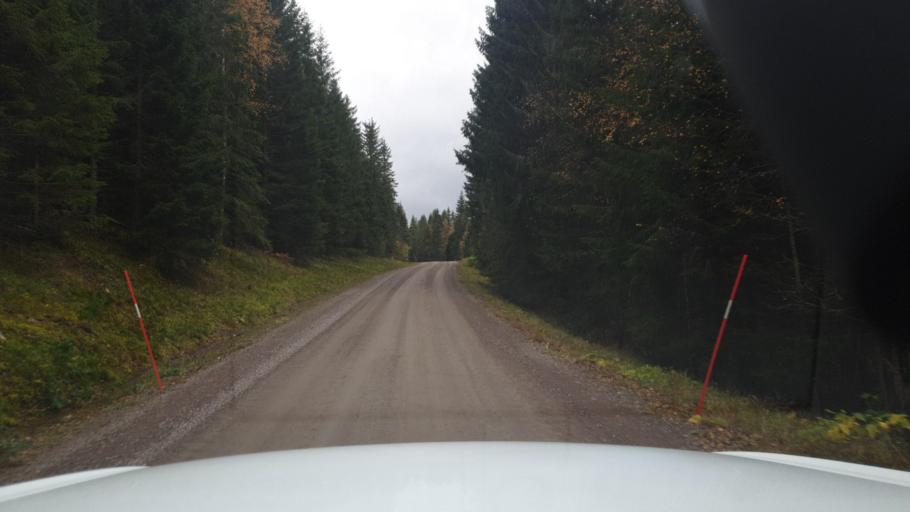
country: SE
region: Vaermland
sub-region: Sunne Kommun
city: Sunne
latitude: 59.8273
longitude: 12.8975
